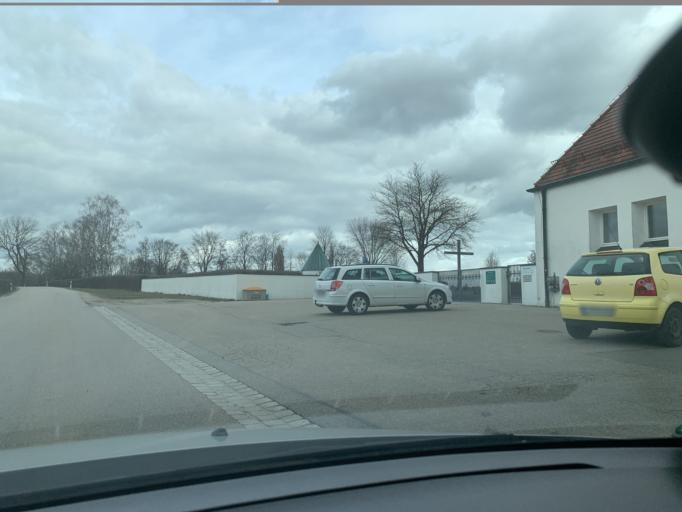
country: DE
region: Bavaria
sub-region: Lower Bavaria
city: Geisenhausen
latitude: 48.4774
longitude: 12.2638
